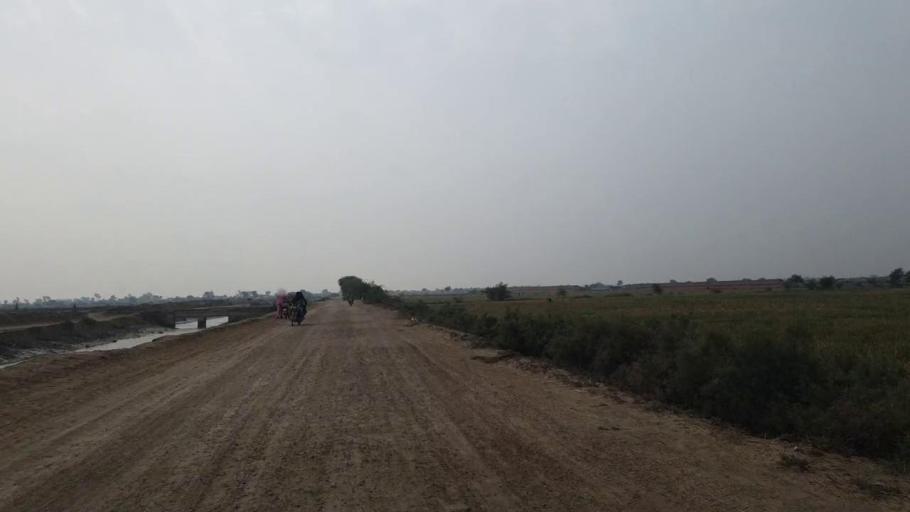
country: PK
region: Sindh
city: Kario
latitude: 24.8921
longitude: 68.5262
